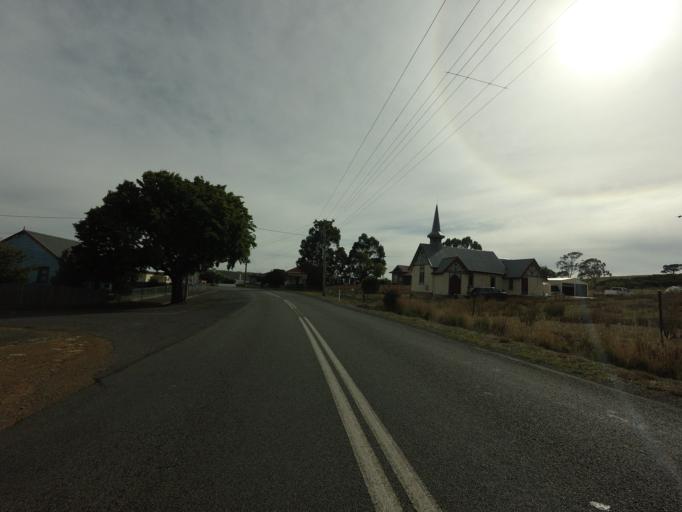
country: AU
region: Tasmania
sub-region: Brighton
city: Bridgewater
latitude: -42.3515
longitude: 147.4070
